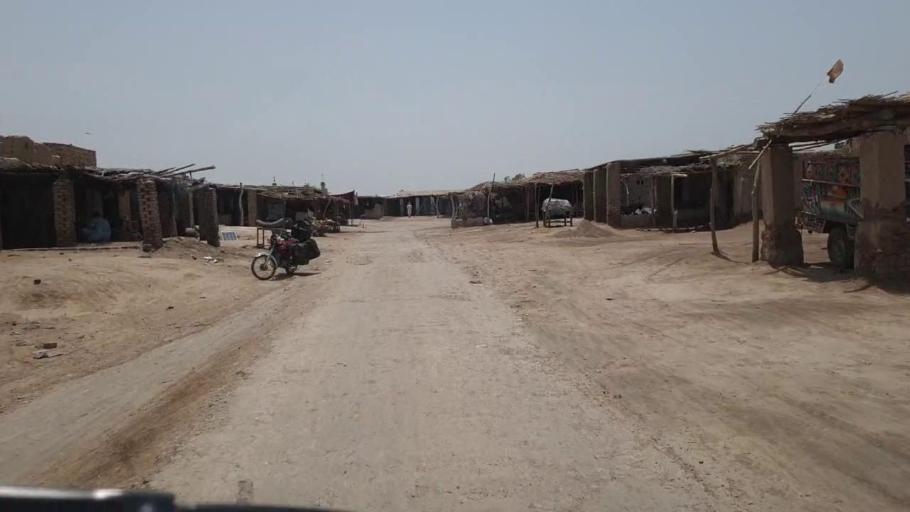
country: PK
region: Sindh
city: Daulatpur
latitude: 26.4616
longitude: 68.1204
